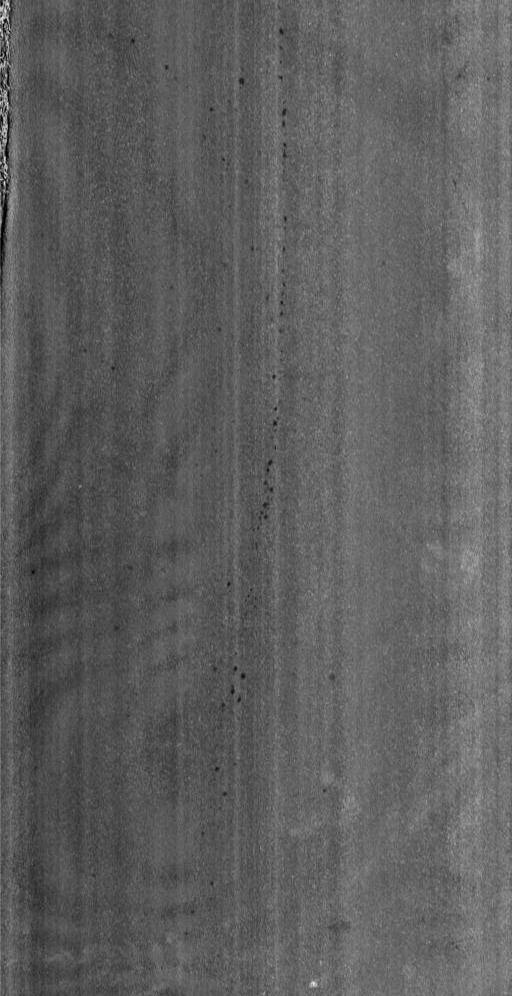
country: US
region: Vermont
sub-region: Chittenden County
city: Hinesburg
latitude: 44.3638
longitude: -73.1995
